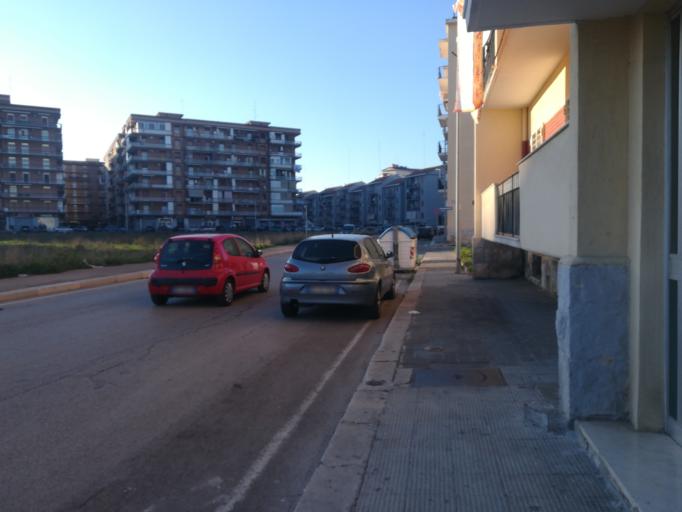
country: IT
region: Apulia
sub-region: Provincia di Bari
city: San Paolo
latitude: 41.1177
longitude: 16.7921
